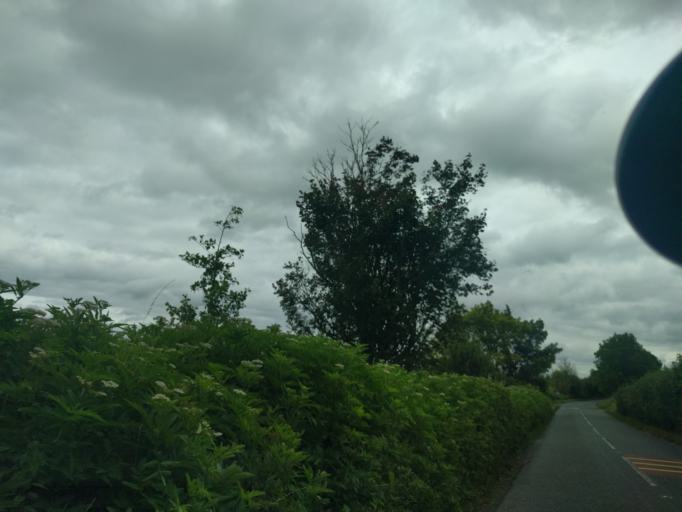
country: GB
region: England
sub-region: Wiltshire
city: Edington
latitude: 51.2792
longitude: -2.0949
